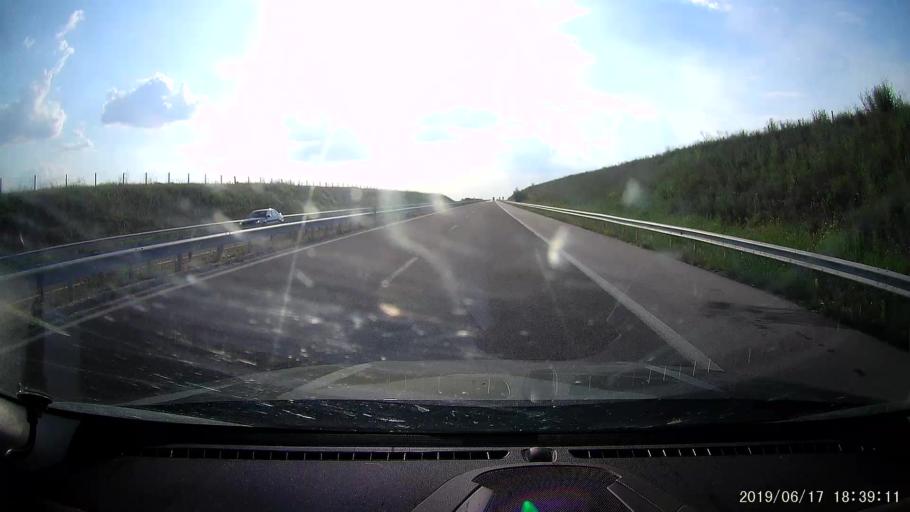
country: BG
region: Stara Zagora
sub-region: Obshtina Chirpan
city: Chirpan
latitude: 42.1427
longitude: 25.3149
